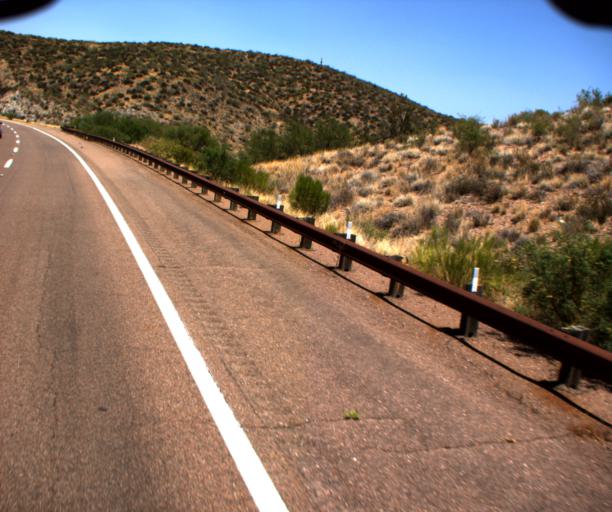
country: US
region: Arizona
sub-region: Gila County
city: Tonto Basin
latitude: 33.9816
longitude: -111.3131
